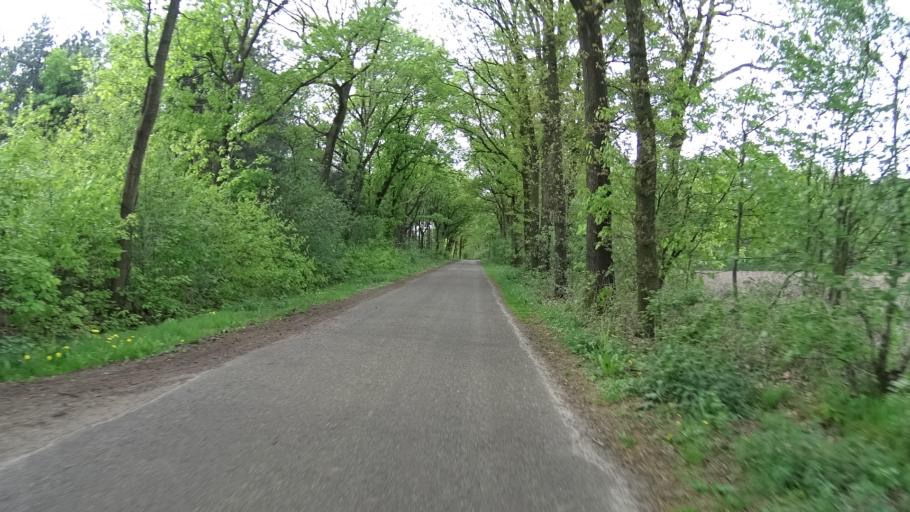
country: NL
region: North Brabant
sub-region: Gemeente Veghel
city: Erp
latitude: 51.6156
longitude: 5.6256
